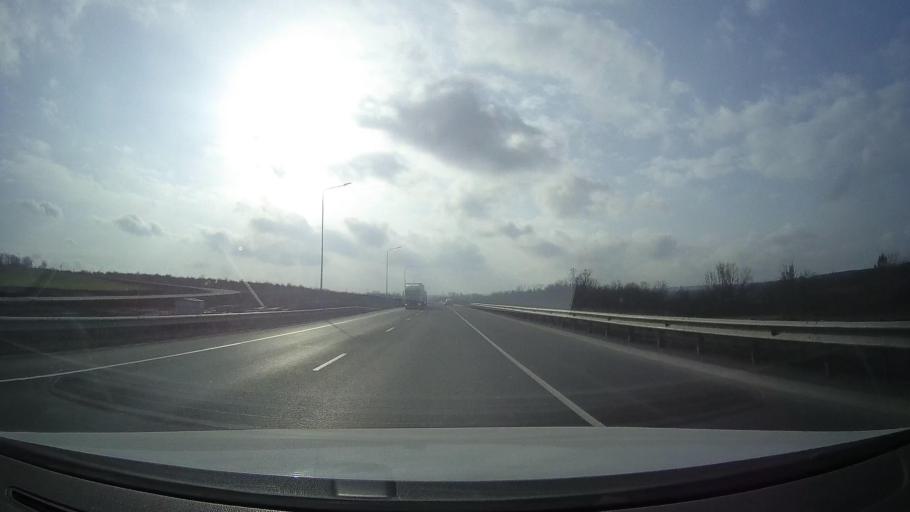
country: RU
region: Rostov
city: Grushevskaya
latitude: 47.4261
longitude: 39.8651
